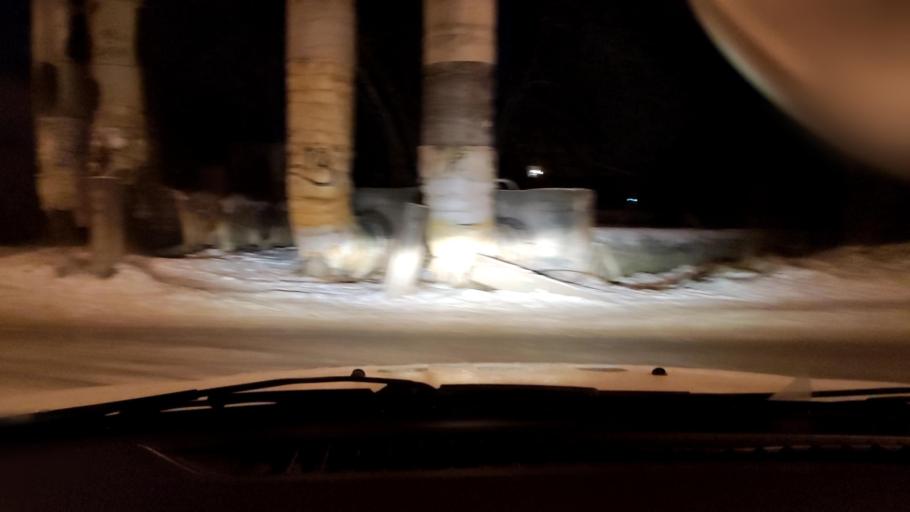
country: RU
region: Perm
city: Overyata
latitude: 58.0107
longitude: 55.9422
